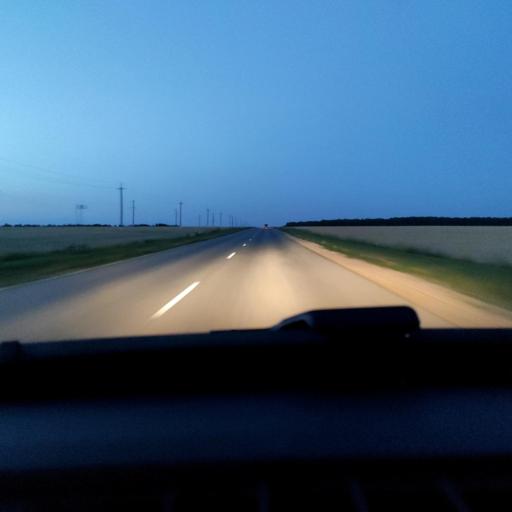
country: RU
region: Lipetsk
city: Zadonsk
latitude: 52.3026
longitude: 38.8637
